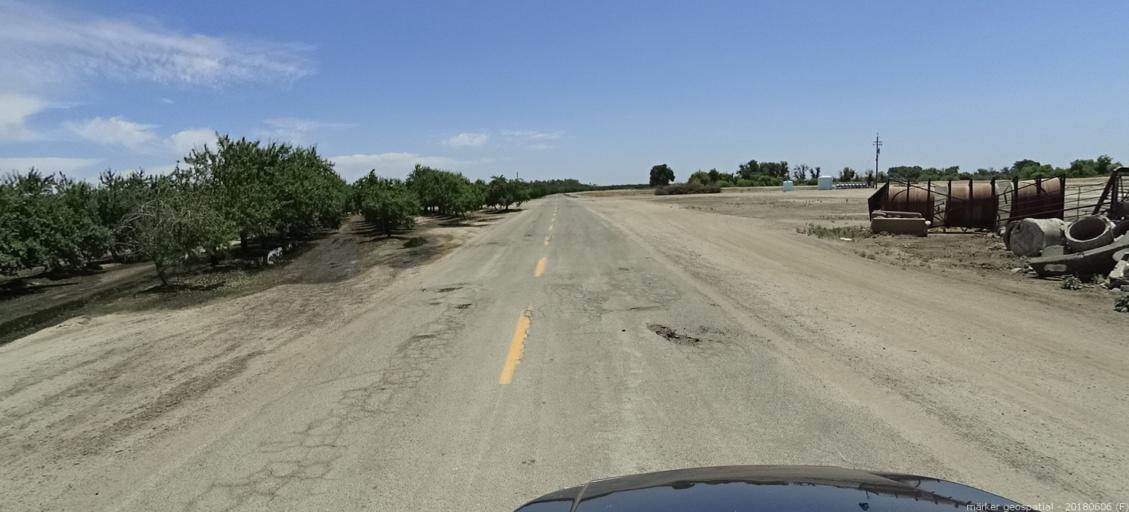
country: US
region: California
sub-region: Fresno County
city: Firebaugh
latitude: 36.8420
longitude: -120.4138
